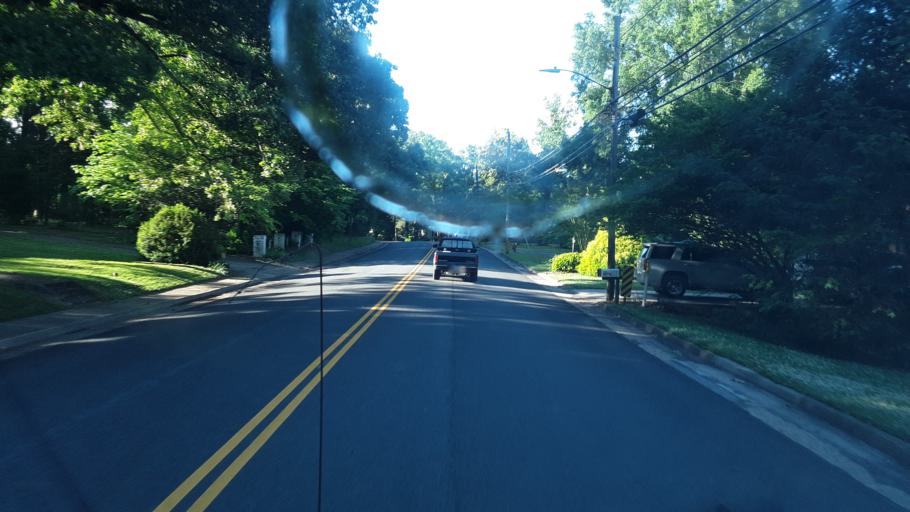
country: US
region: Virginia
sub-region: Pittsylvania County
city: Chatham
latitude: 36.8133
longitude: -79.3949
